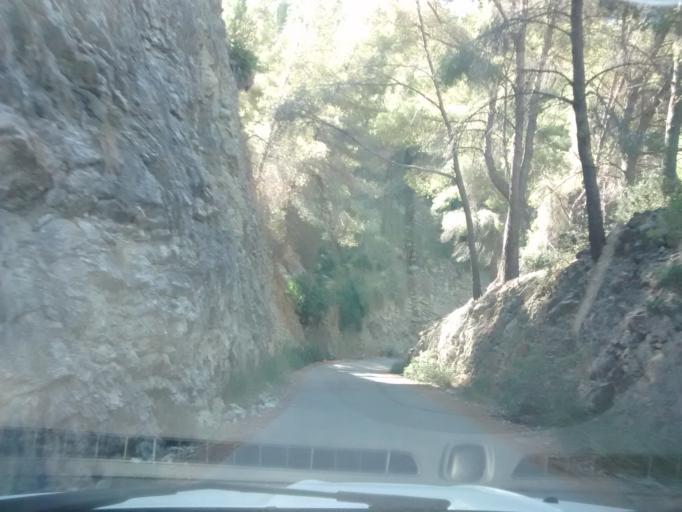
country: ES
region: Balearic Islands
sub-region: Illes Balears
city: Port d'Alcudia
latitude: 39.8777
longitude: 3.1753
